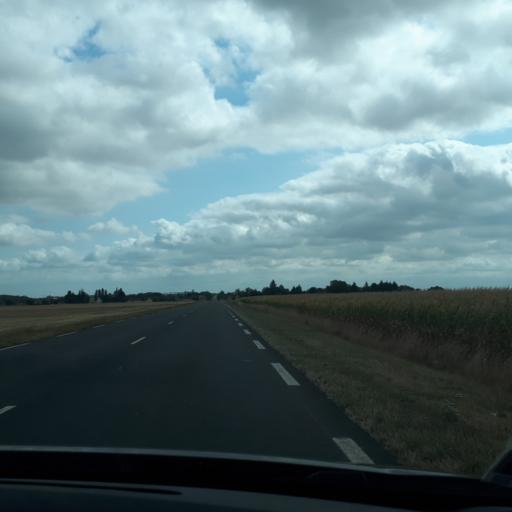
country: FR
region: Centre
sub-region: Departement du Loir-et-Cher
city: Ouzouer-le-Marche
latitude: 47.9052
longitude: 1.4791
